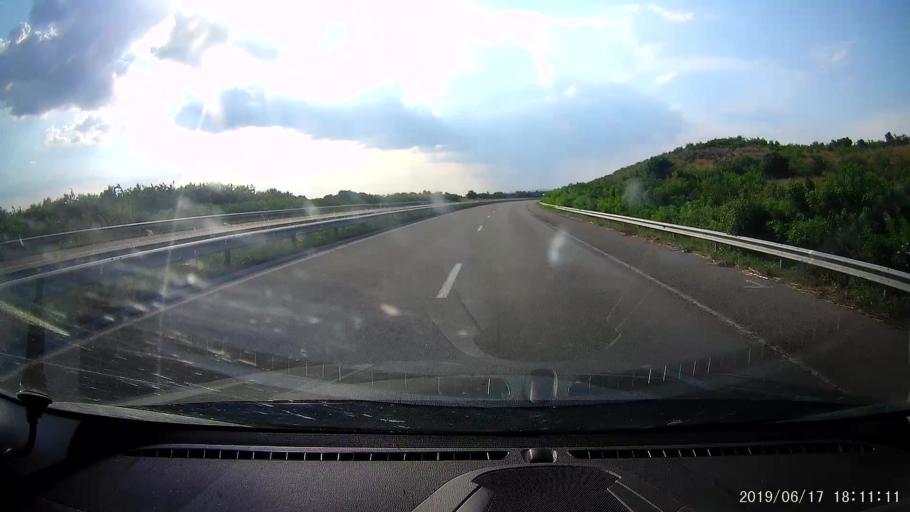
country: BG
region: Khaskovo
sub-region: Obshtina Lyubimets
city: Lyubimets
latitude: 41.8801
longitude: 26.0567
